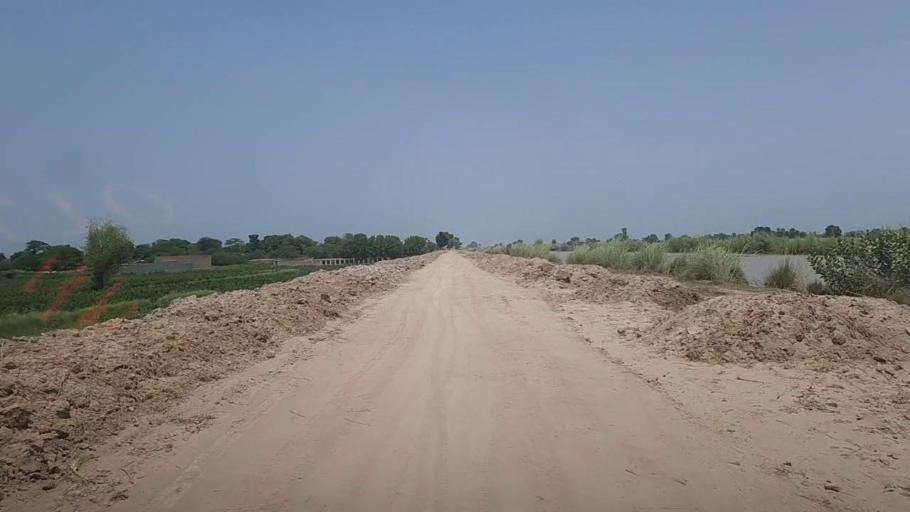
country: PK
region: Sindh
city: Pad Idan
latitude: 26.7886
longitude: 68.2766
